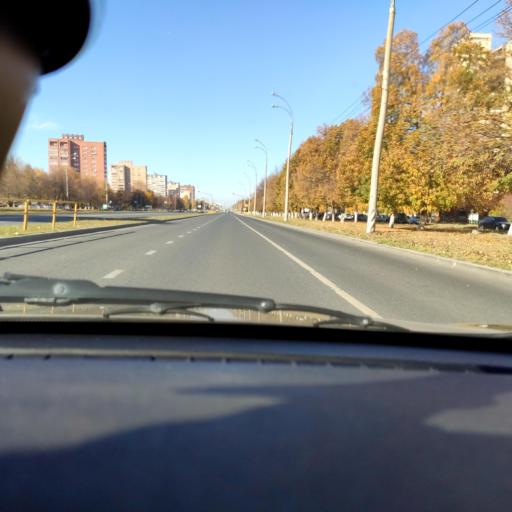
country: RU
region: Samara
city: Tol'yatti
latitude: 53.5255
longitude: 49.3210
